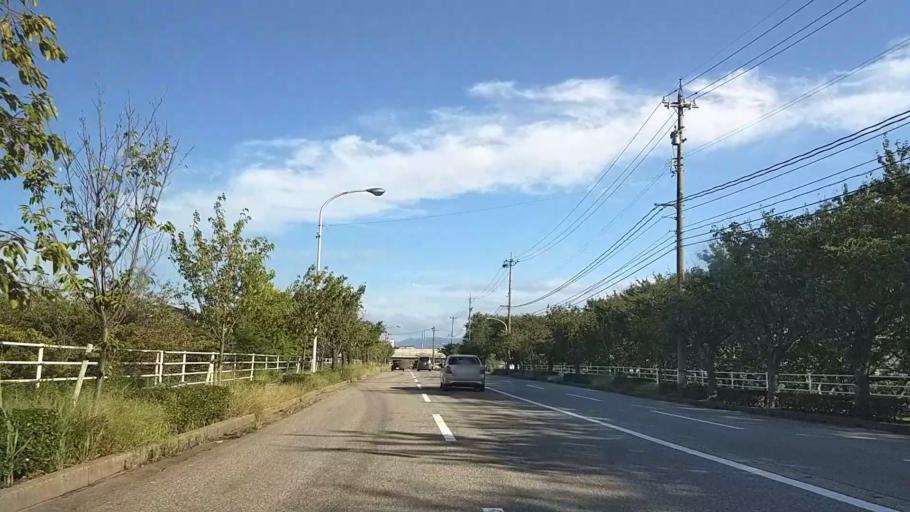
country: JP
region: Ishikawa
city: Kanazawa-shi
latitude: 36.5690
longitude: 136.6372
